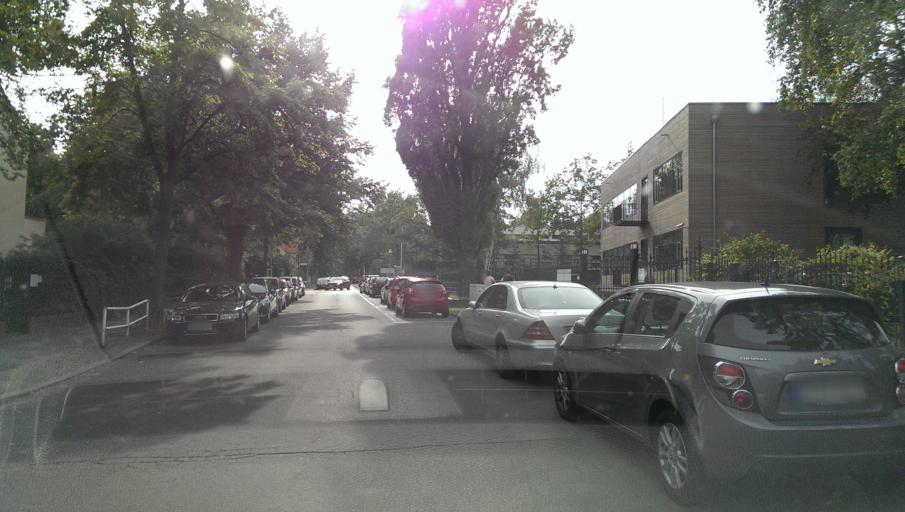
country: DE
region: Berlin
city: Zehlendorf Bezirk
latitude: 52.4345
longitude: 13.2556
